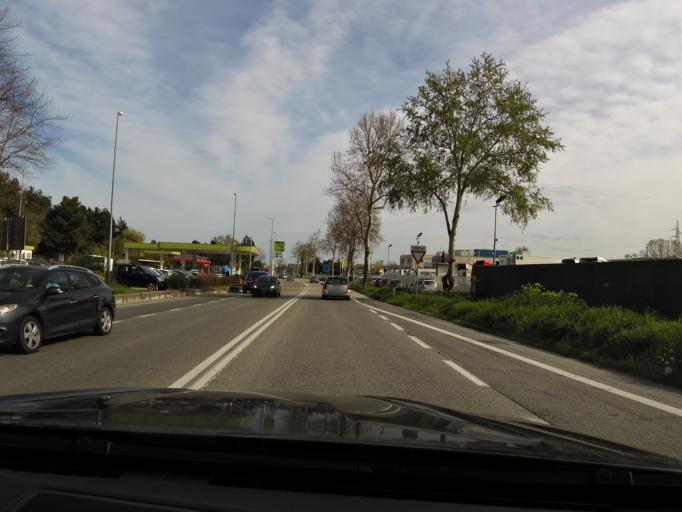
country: IT
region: The Marches
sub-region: Provincia di Macerata
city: Porto Recanati
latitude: 43.4372
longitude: 13.6425
